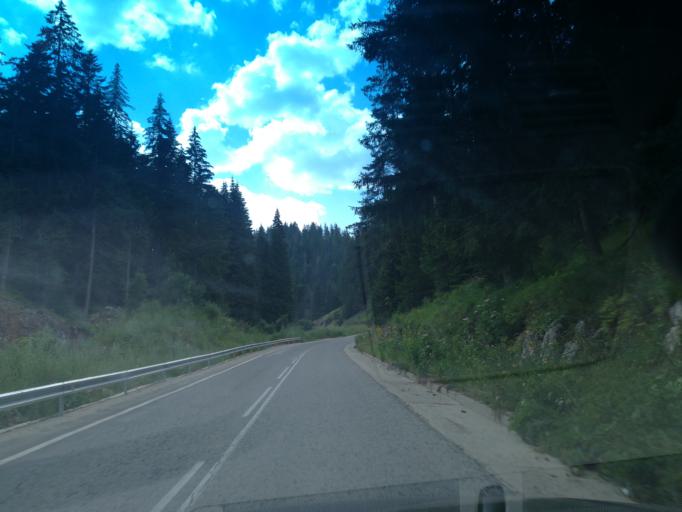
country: BG
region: Smolyan
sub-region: Obshtina Smolyan
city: Smolyan
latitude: 41.6583
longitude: 24.7074
